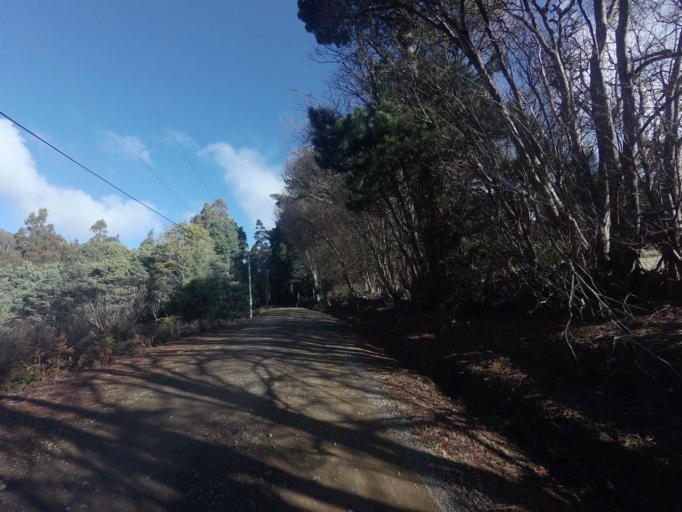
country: AU
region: Tasmania
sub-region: Glenorchy
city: Berriedale
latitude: -42.8565
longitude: 147.1670
